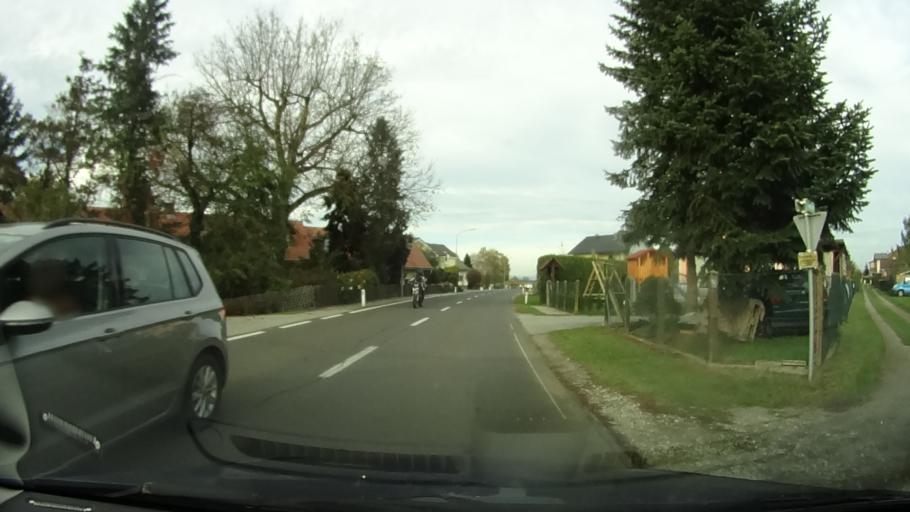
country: AT
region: Styria
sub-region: Politischer Bezirk Graz-Umgebung
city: Wundschuh
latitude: 46.9390
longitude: 15.4445
